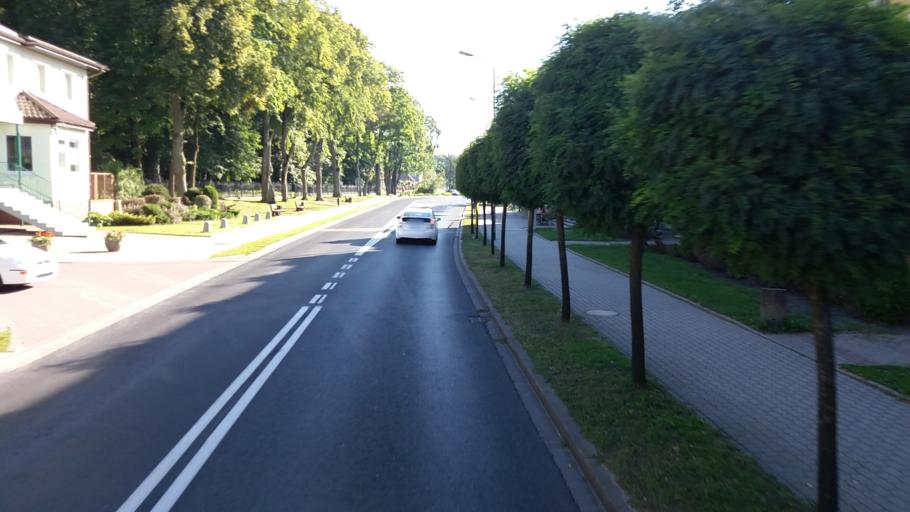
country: PL
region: West Pomeranian Voivodeship
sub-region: Powiat drawski
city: Kalisz Pomorski
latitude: 53.2948
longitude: 15.9031
